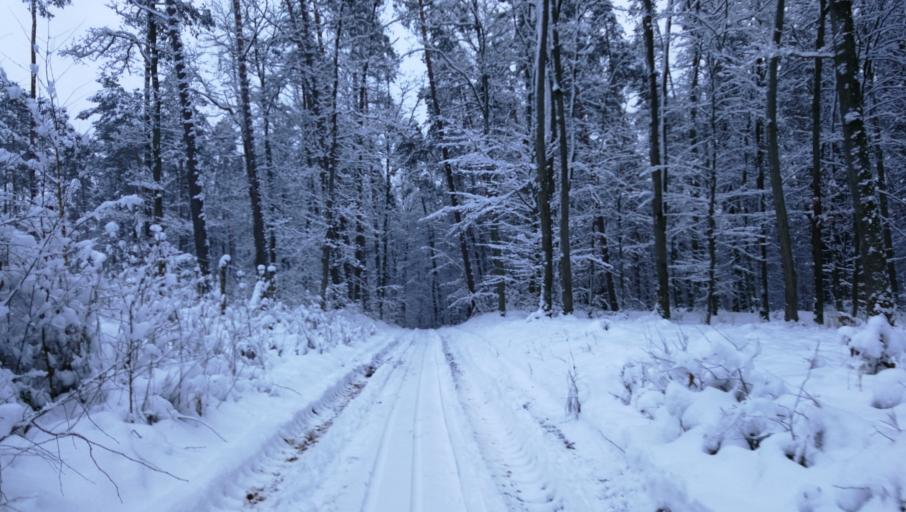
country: PL
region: Kujawsko-Pomorskie
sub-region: Powiat brodnicki
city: Gorzno
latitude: 53.2056
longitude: 19.6969
